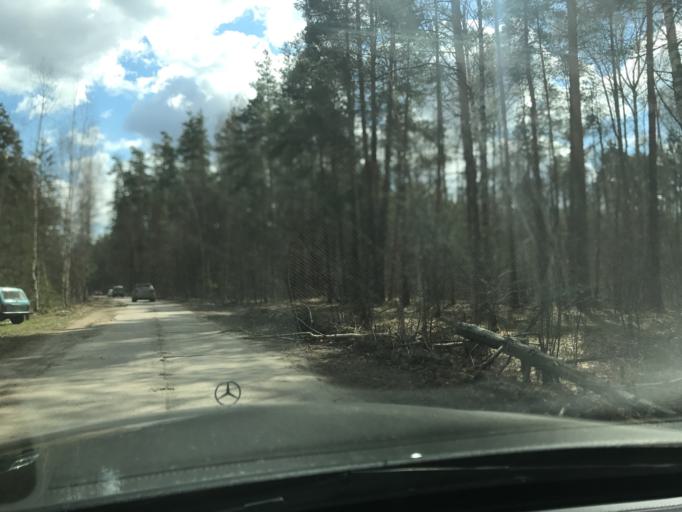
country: RU
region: Moskovskaya
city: Vereya
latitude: 55.8402
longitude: 39.1088
